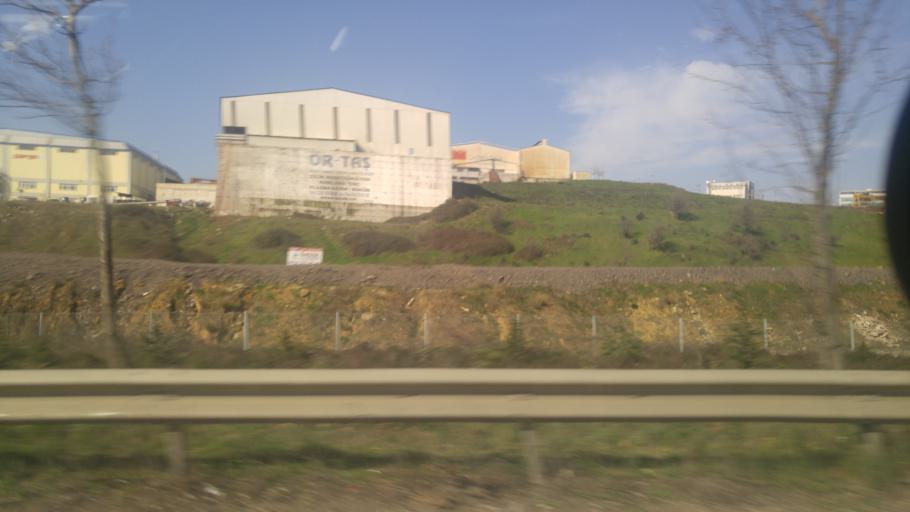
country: TR
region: Kocaeli
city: Balcik
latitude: 40.8438
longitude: 29.3741
